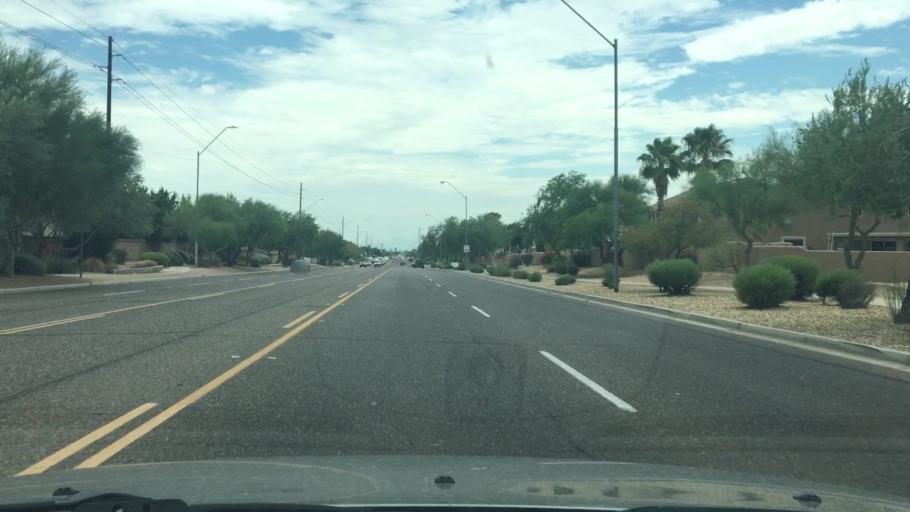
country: US
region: Arizona
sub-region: Maricopa County
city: Sun City
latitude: 33.7176
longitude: -112.2032
